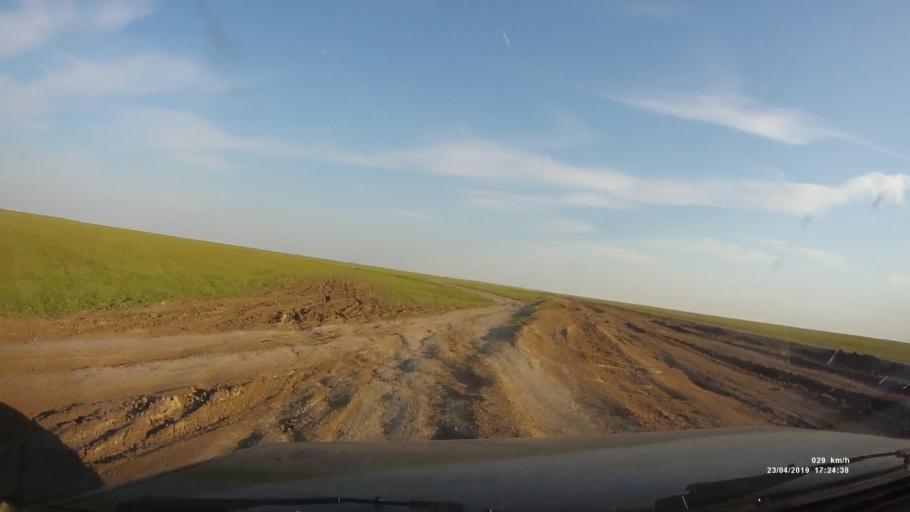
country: RU
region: Kalmykiya
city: Priyutnoye
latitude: 46.1563
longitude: 43.5088
